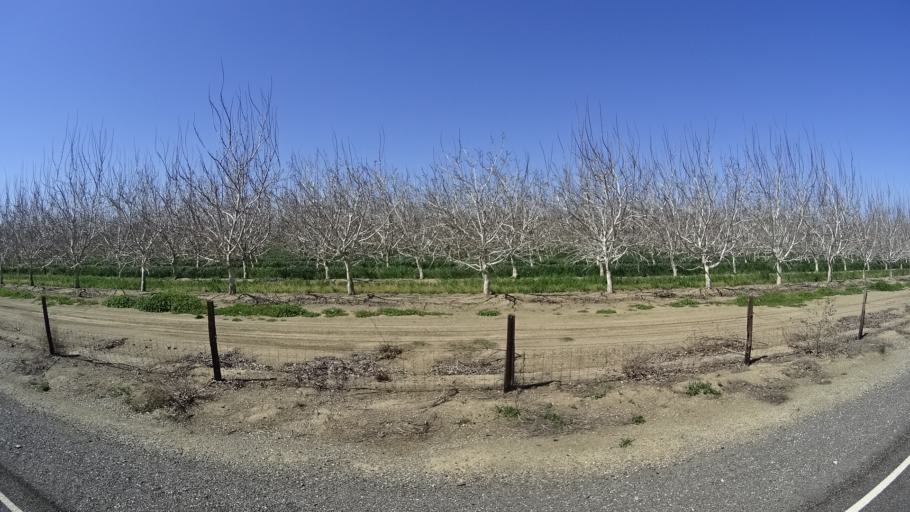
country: US
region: California
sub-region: Glenn County
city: Willows
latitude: 39.6210
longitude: -122.2500
